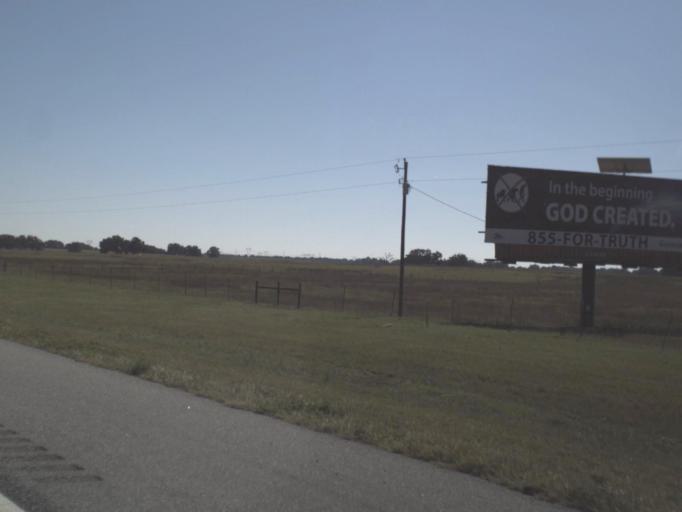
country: US
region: Florida
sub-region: Sumter County
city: Wildwood
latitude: 28.7846
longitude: -81.9801
